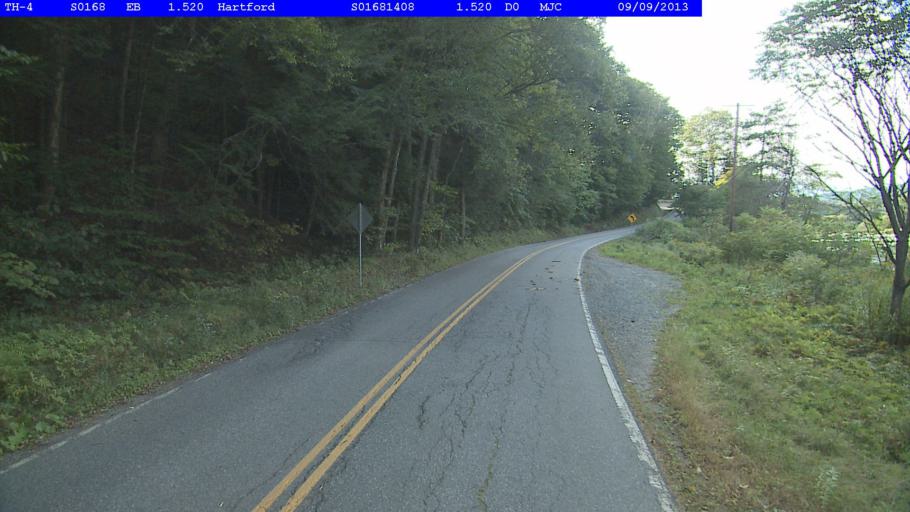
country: US
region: Vermont
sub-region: Windsor County
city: White River Junction
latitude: 43.6417
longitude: -72.4011
